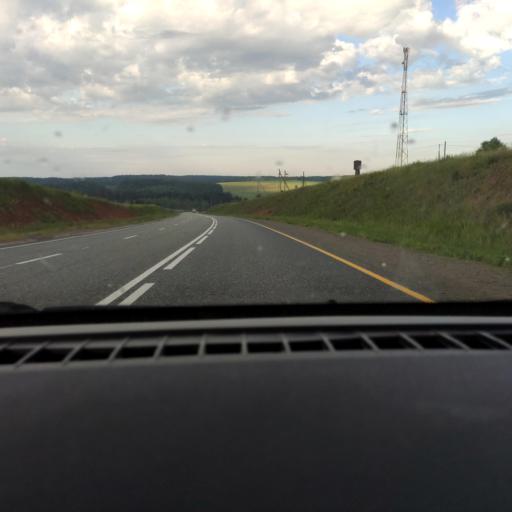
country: RU
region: Udmurtiya
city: Votkinsk
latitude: 57.2389
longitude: 54.1988
